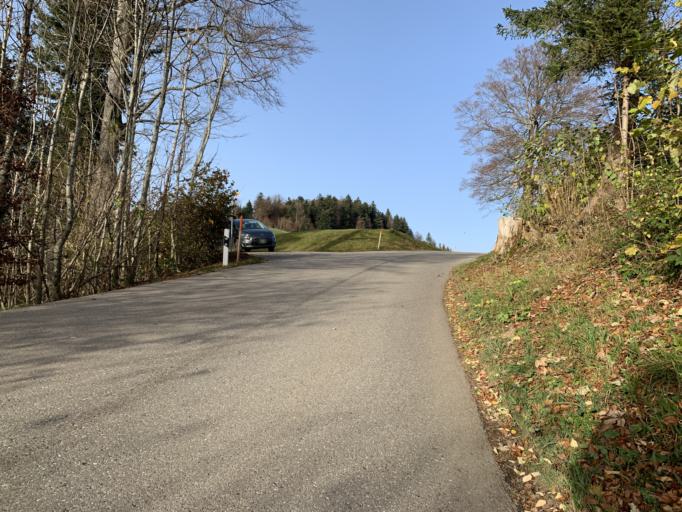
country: CH
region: Zurich
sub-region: Bezirk Hinwil
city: Hadlikon
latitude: 47.3061
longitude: 8.8867
